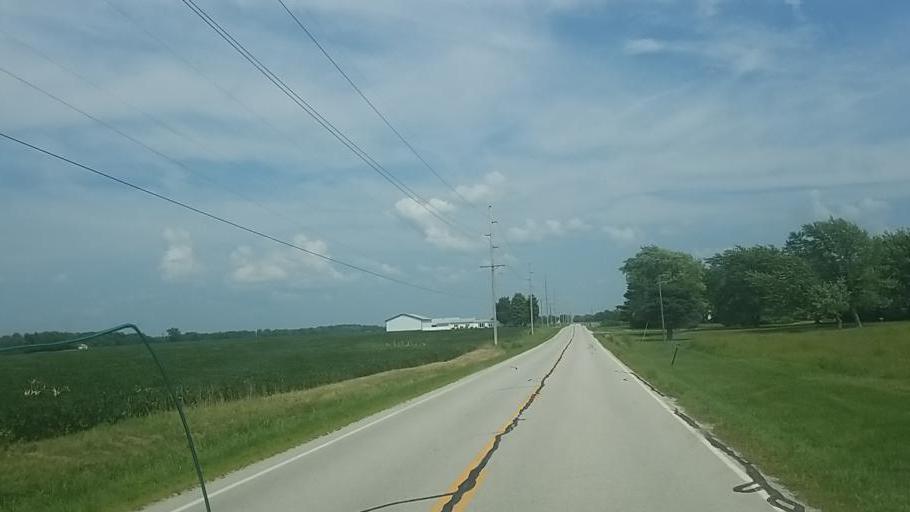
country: US
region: Ohio
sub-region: Hardin County
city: Forest
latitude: 40.7819
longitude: -83.5489
